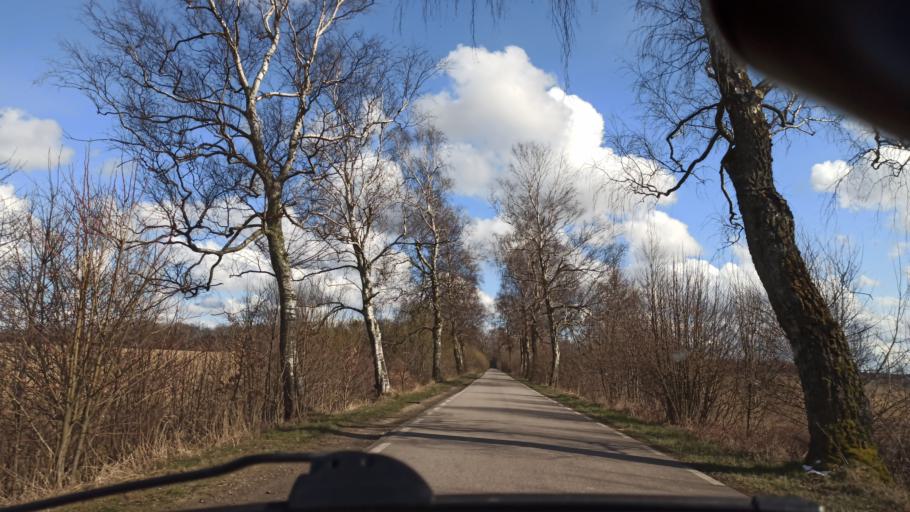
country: PL
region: Warmian-Masurian Voivodeship
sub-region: Powiat elblaski
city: Tolkmicko
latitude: 54.2641
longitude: 19.4866
